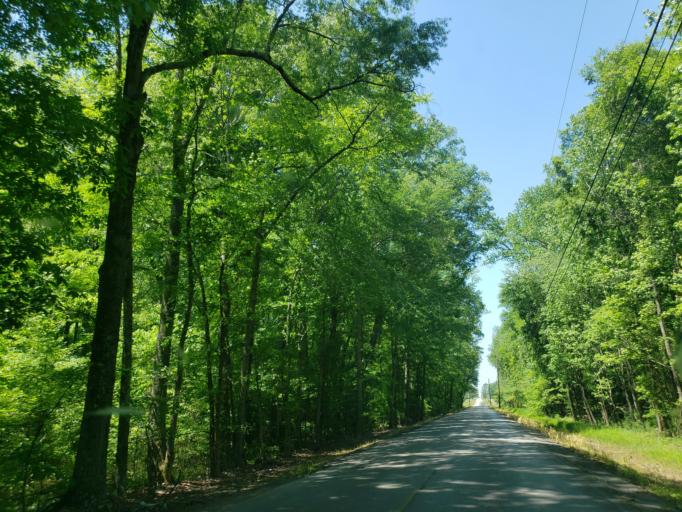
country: US
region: Alabama
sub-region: Madison County
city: Hazel Green
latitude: 34.9617
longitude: -86.5886
